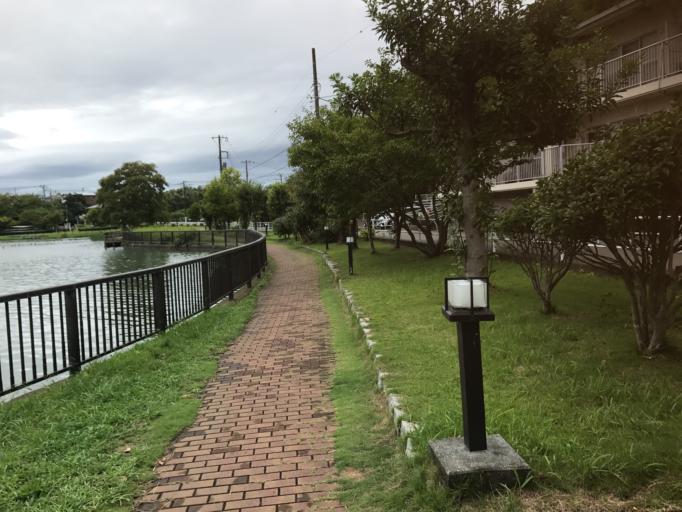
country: JP
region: Shizuoka
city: Numazu
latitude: 35.1299
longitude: 138.8806
